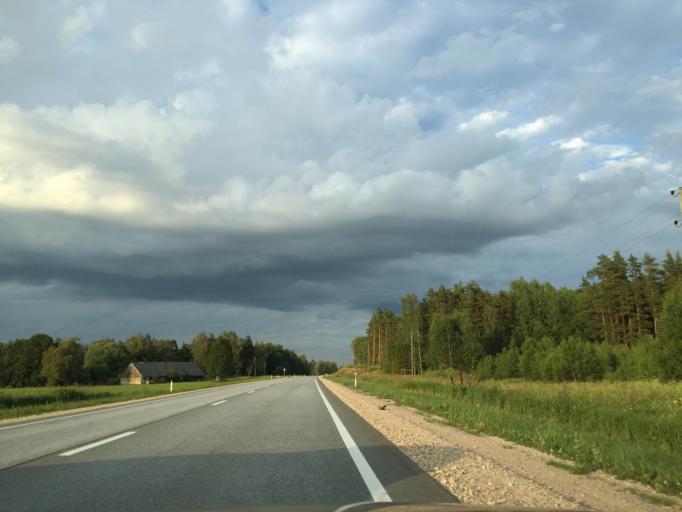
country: LV
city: Tireli
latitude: 56.8905
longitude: 23.6845
